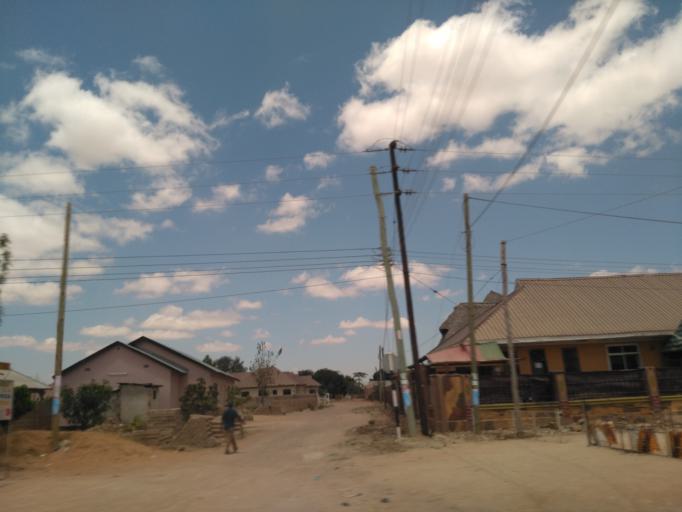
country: TZ
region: Dodoma
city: Kisasa
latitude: -6.1652
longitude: 35.7888
